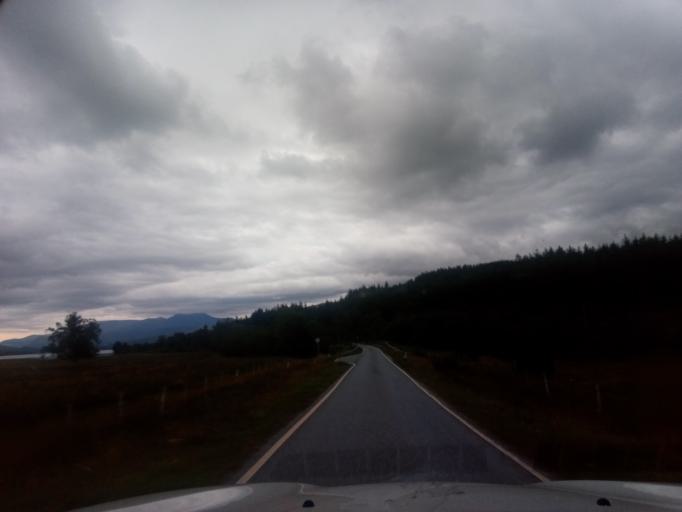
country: GB
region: Scotland
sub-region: Highland
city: Fort William
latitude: 56.8563
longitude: -5.3473
